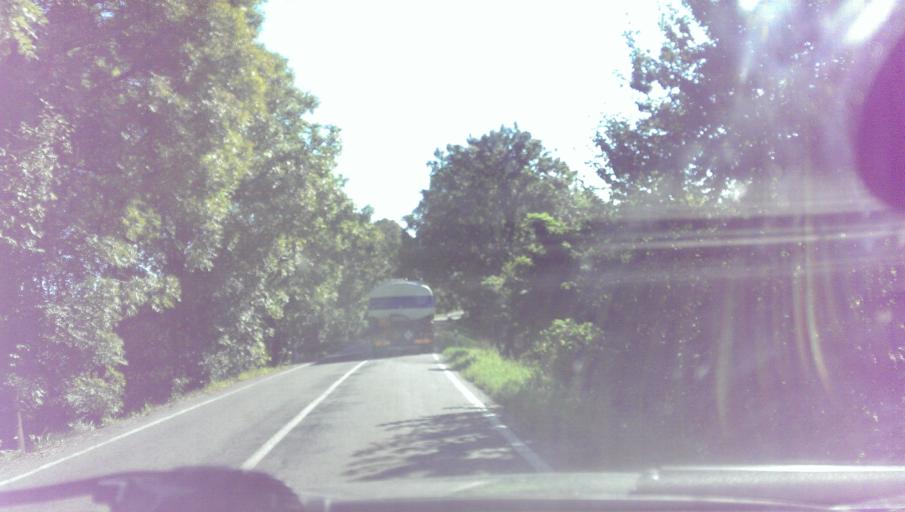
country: CZ
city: Brusperk
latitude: 49.6879
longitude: 18.2022
